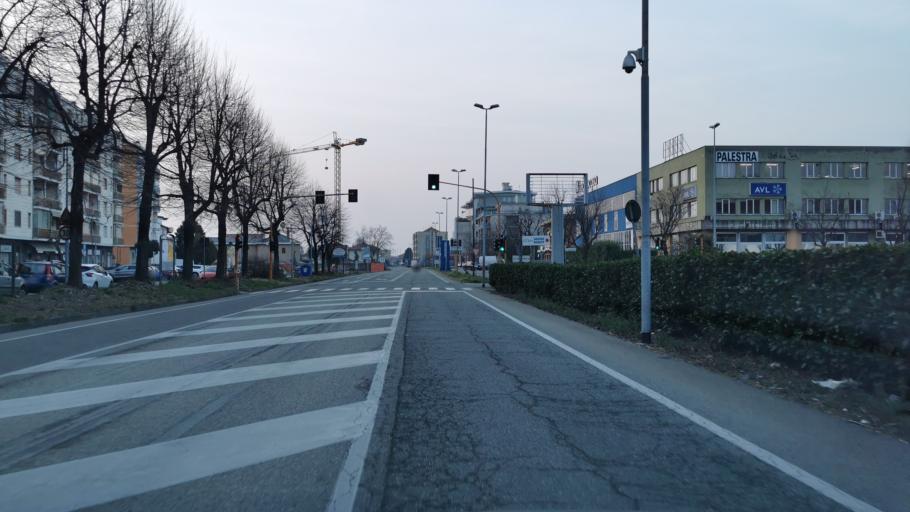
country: IT
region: Piedmont
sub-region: Provincia di Torino
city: Borgaro Torinese
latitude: 45.1552
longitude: 7.6547
